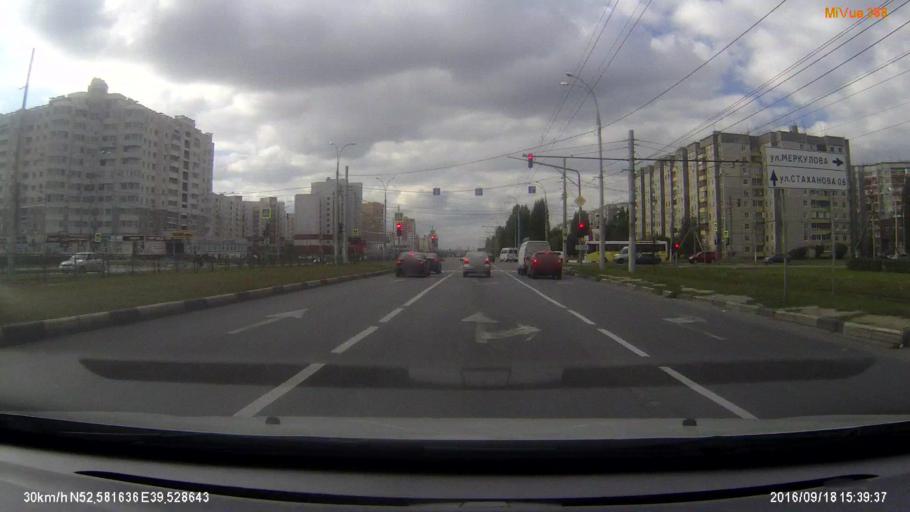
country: RU
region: Lipetsk
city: Syrskoye
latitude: 52.5817
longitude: 39.5286
